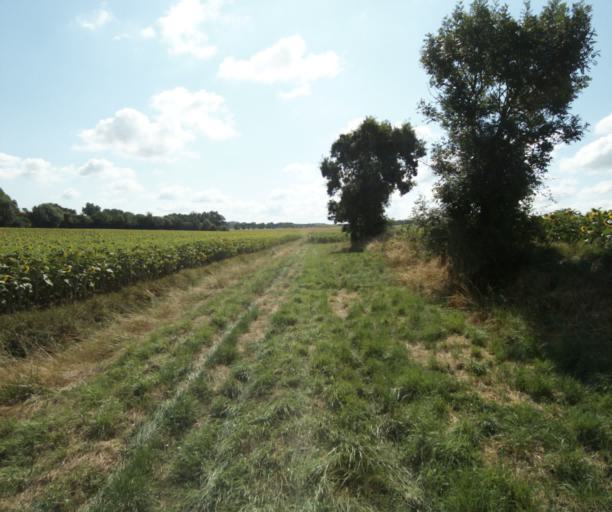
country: FR
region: Midi-Pyrenees
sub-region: Departement de la Haute-Garonne
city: Avignonet-Lauragais
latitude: 43.4458
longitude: 1.7926
